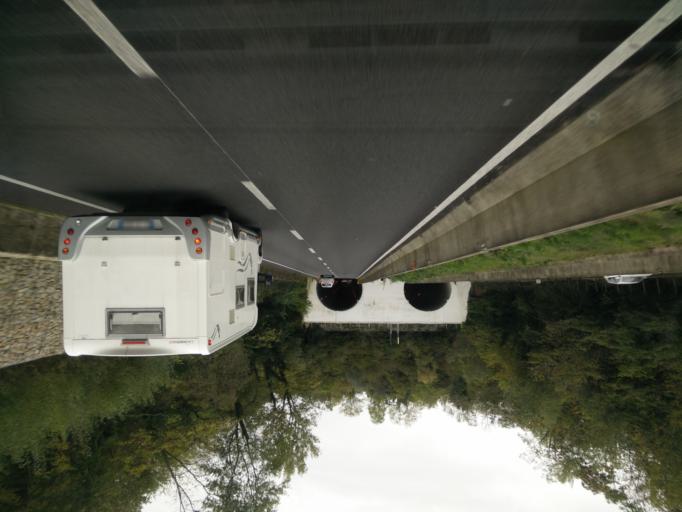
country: IT
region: Tuscany
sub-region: Province of Florence
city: San Casciano in Val di Pesa
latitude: 43.6522
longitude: 11.1909
